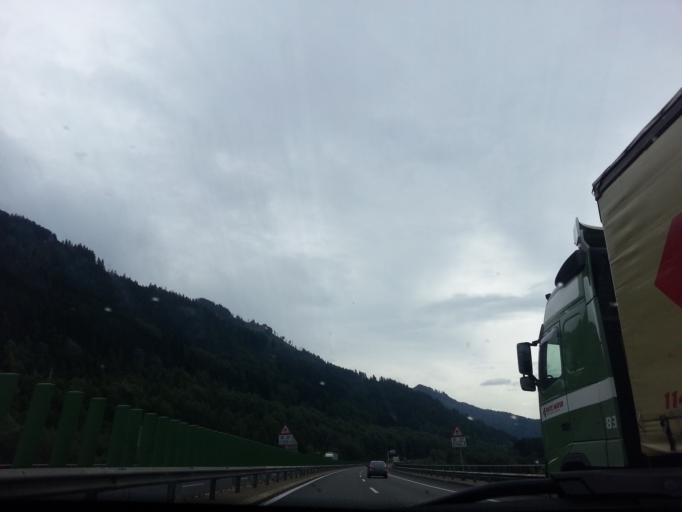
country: AT
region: Styria
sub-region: Politischer Bezirk Liezen
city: Treglwang
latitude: 47.4739
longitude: 14.6011
